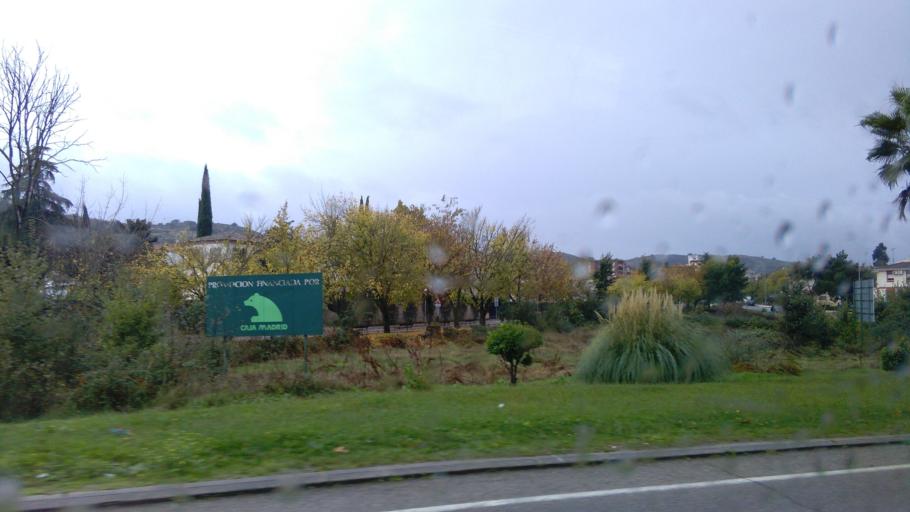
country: ES
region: Extremadura
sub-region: Provincia de Caceres
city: Navalmoral de la Mata
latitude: 39.8915
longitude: -5.5288
